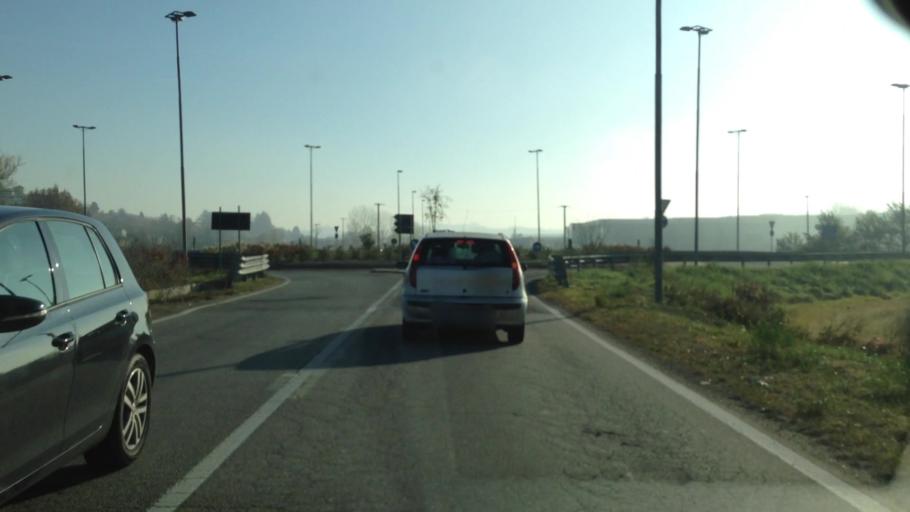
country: IT
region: Piedmont
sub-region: Provincia di Asti
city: Vigliano d'Asti
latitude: 44.8227
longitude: 8.2247
